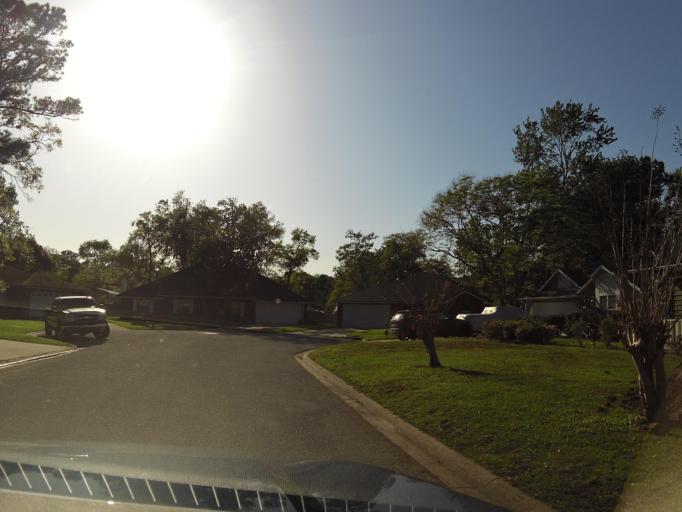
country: US
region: Florida
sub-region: Duval County
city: Jacksonville
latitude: 30.2732
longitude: -81.5800
